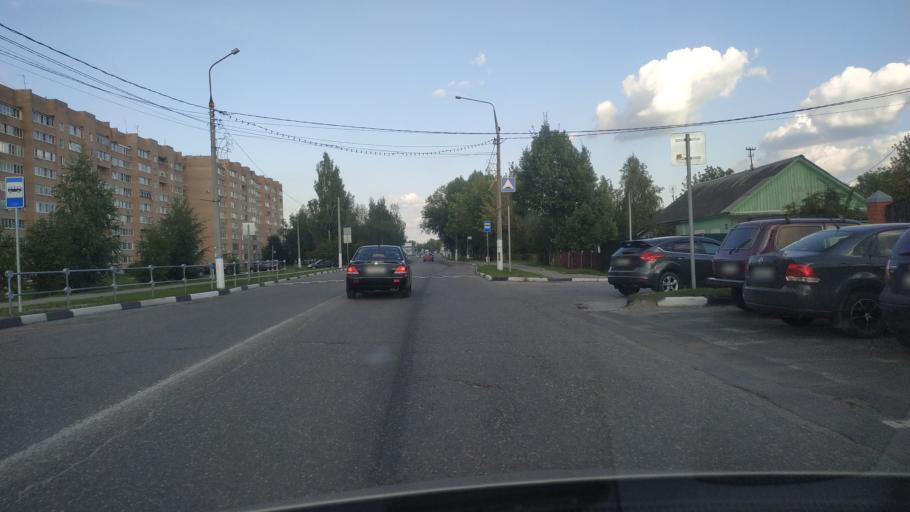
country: RU
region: Moskovskaya
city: Shatura
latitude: 55.5755
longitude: 39.5144
